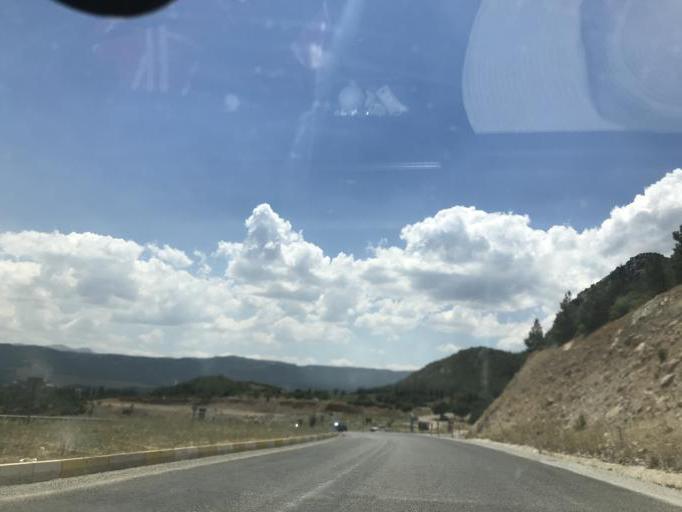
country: TR
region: Denizli
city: Honaz
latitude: 37.7020
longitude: 29.2009
